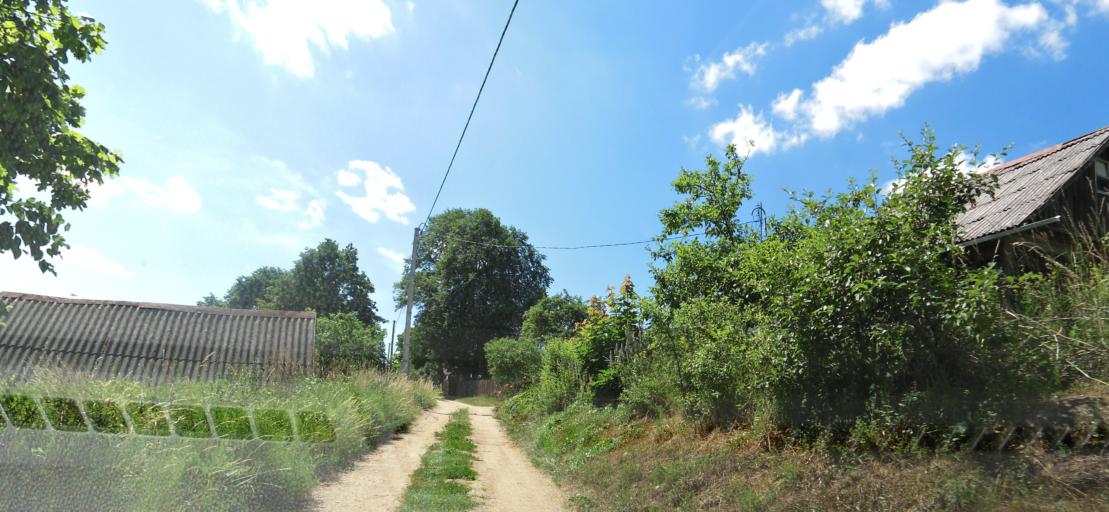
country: LT
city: Nemencine
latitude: 54.8707
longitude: 25.5711
